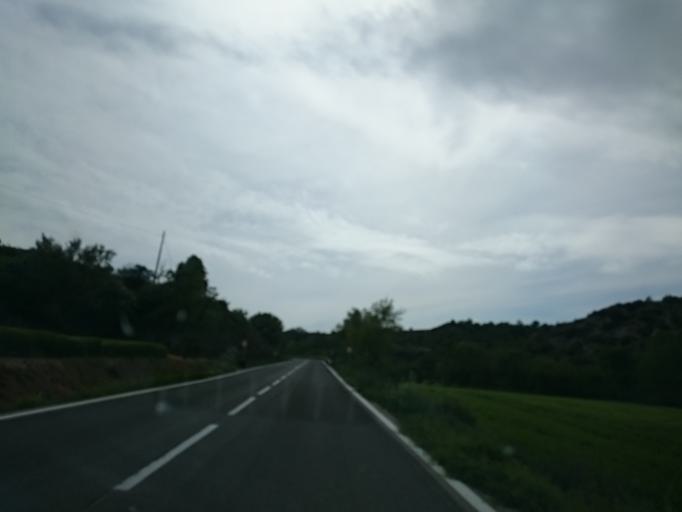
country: ES
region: Catalonia
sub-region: Provincia de Lleida
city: Ivorra
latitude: 41.7908
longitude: 1.3942
